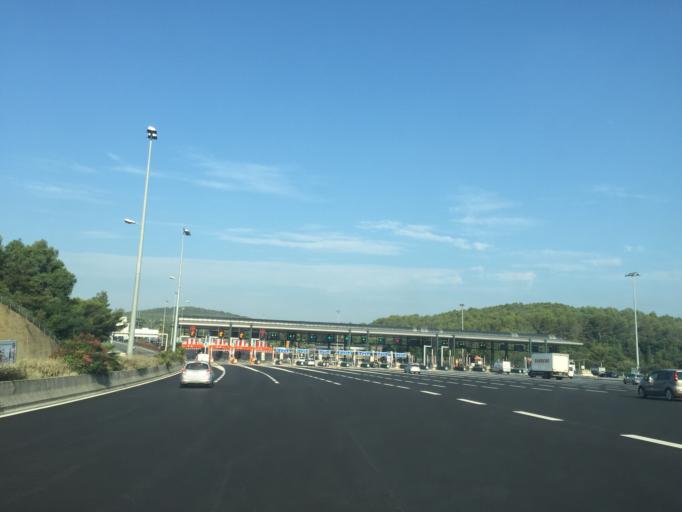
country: FR
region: Provence-Alpes-Cote d'Azur
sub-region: Departement des Alpes-Maritimes
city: Vallauris
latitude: 43.6044
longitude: 7.0683
